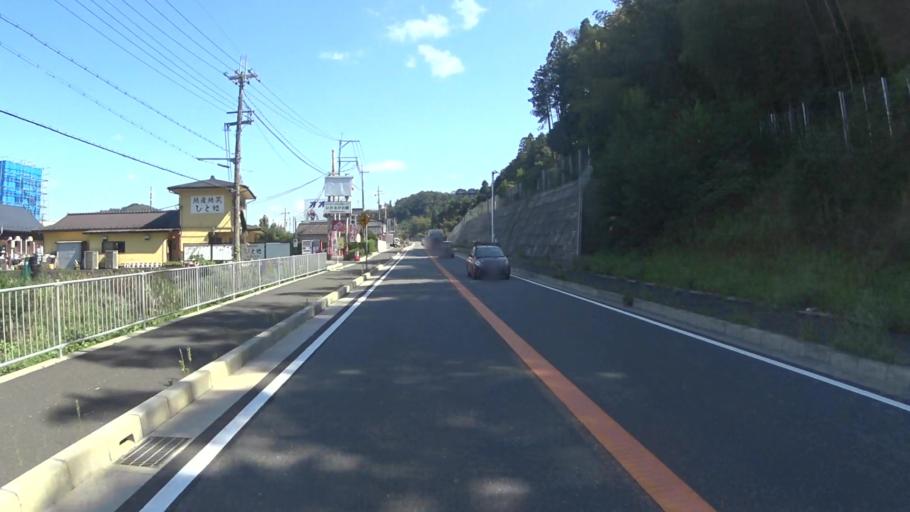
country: JP
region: Kyoto
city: Ayabe
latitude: 35.3022
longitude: 135.2706
